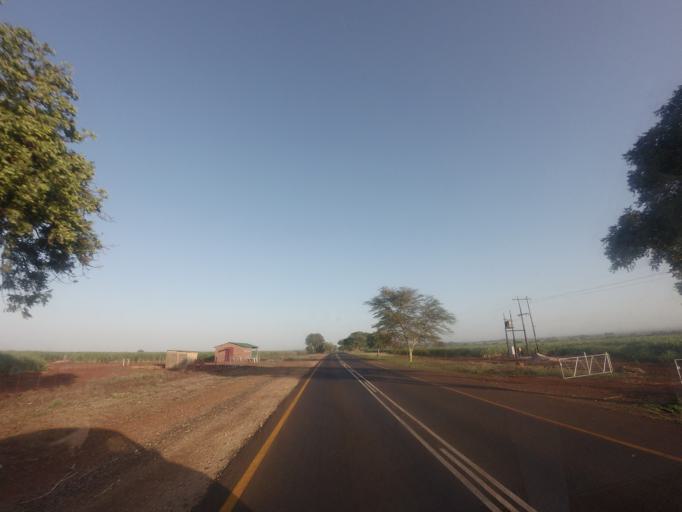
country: ZA
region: Mpumalanga
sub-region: Ehlanzeni District
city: Komatipoort
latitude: -25.3968
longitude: 31.9179
